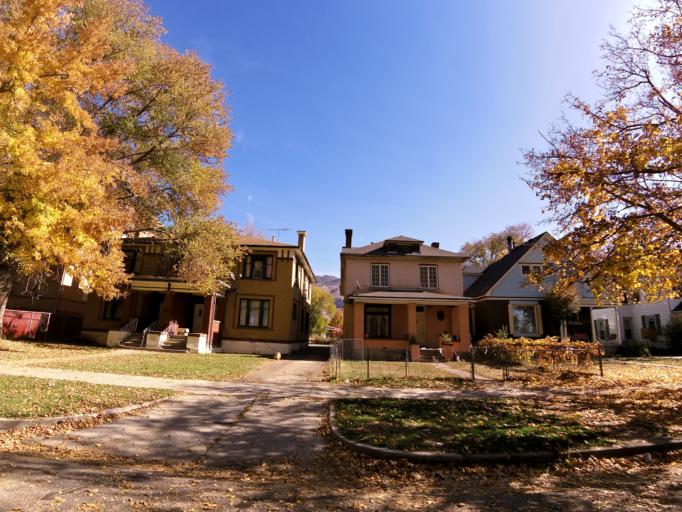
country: US
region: Utah
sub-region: Weber County
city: Ogden
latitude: 41.2214
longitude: -111.9620
